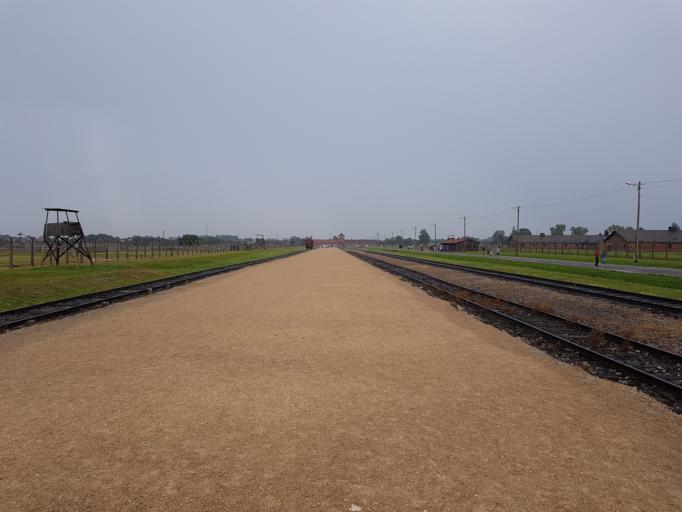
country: PL
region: Lesser Poland Voivodeship
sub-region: Powiat oswiecimski
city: Brzezinka
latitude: 50.0348
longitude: 19.1733
